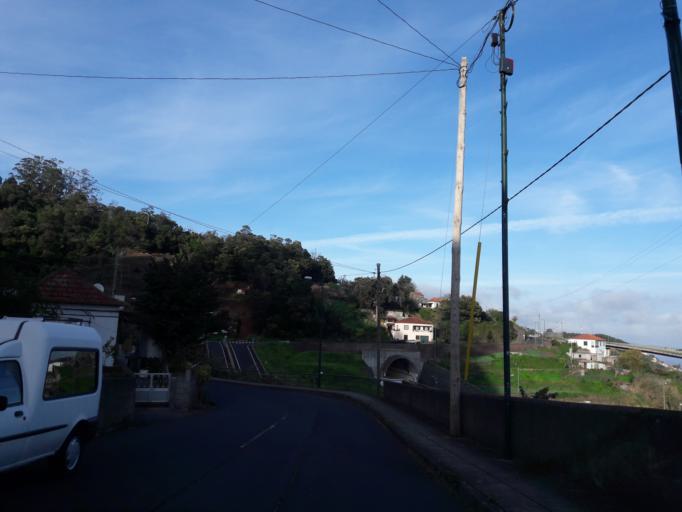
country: PT
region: Madeira
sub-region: Santa Cruz
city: Camacha
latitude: 32.6585
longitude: -16.8526
